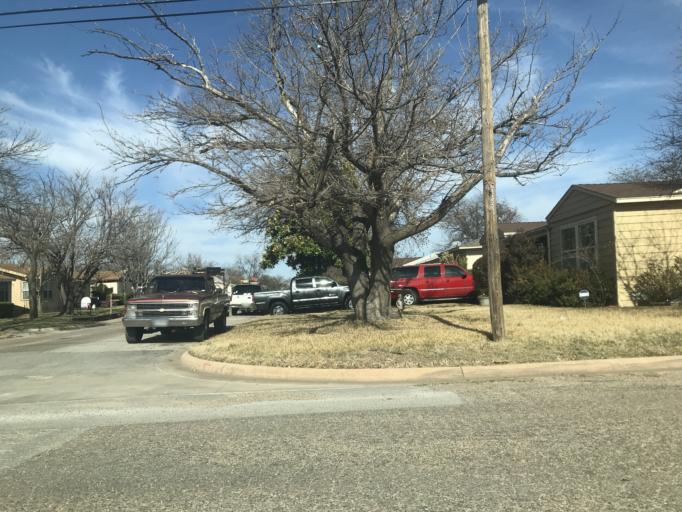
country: US
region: Texas
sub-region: Taylor County
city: Abilene
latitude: 32.4211
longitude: -99.7515
